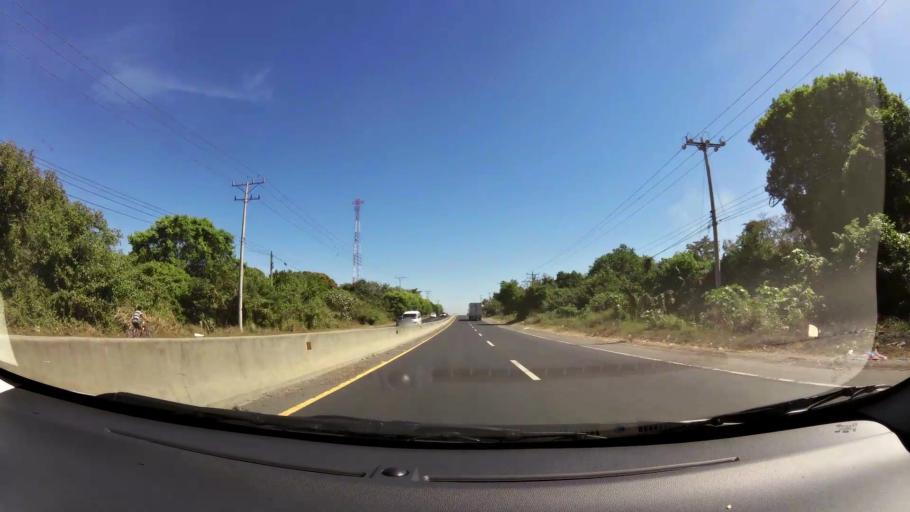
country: SV
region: La Libertad
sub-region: Distrito de Quezaltepeque
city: Quezaltepeque
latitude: 13.8172
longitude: -89.3069
